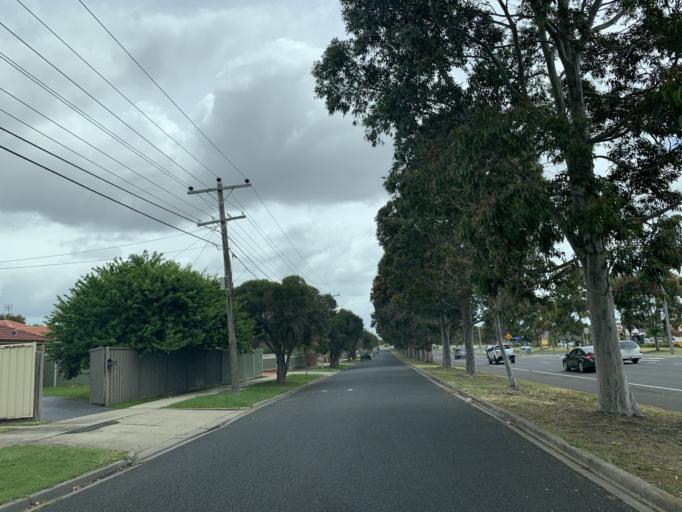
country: AU
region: Victoria
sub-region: Brimbank
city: Kealba
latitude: -37.7429
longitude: 144.8262
